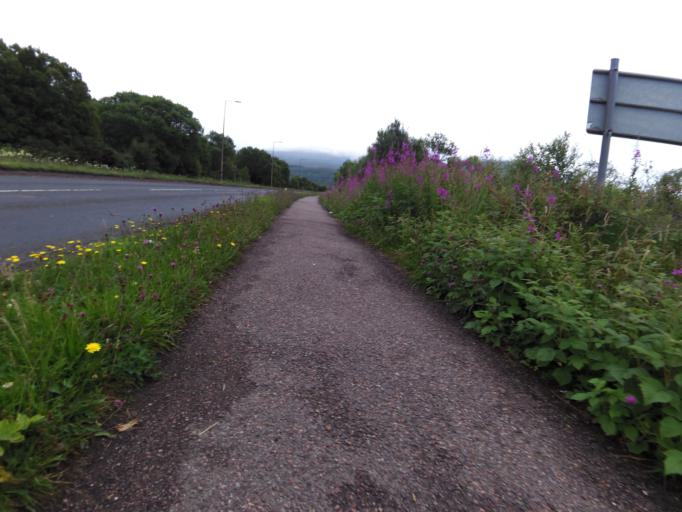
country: GB
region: Scotland
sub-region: Highland
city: Fort William
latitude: 56.8428
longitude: -5.0902
